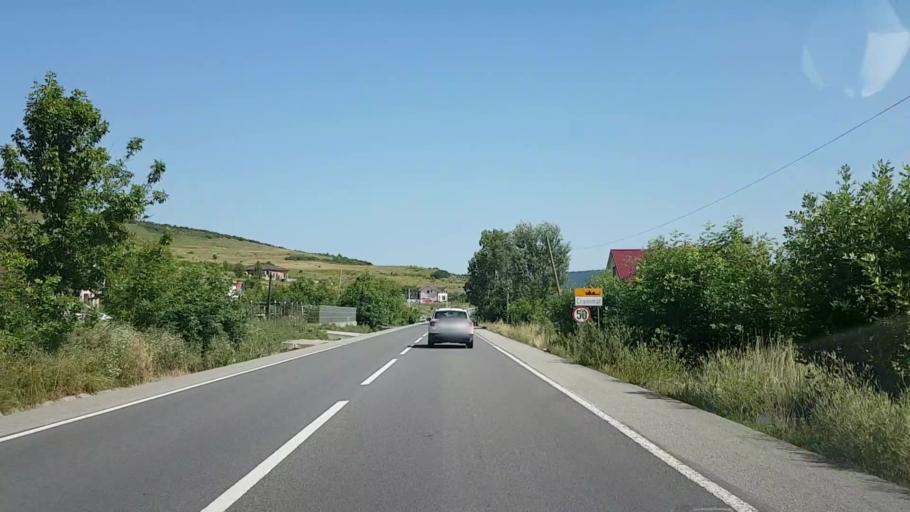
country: RO
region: Bistrita-Nasaud
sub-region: Comuna Sieu-Magherus
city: Sieu-Magherus
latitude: 47.0794
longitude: 24.3940
